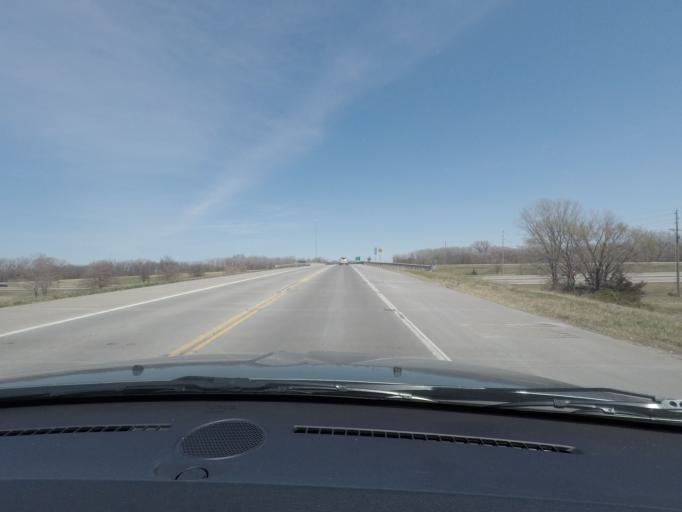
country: US
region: Kansas
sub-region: Lyon County
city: Emporia
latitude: 38.4224
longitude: -96.1817
